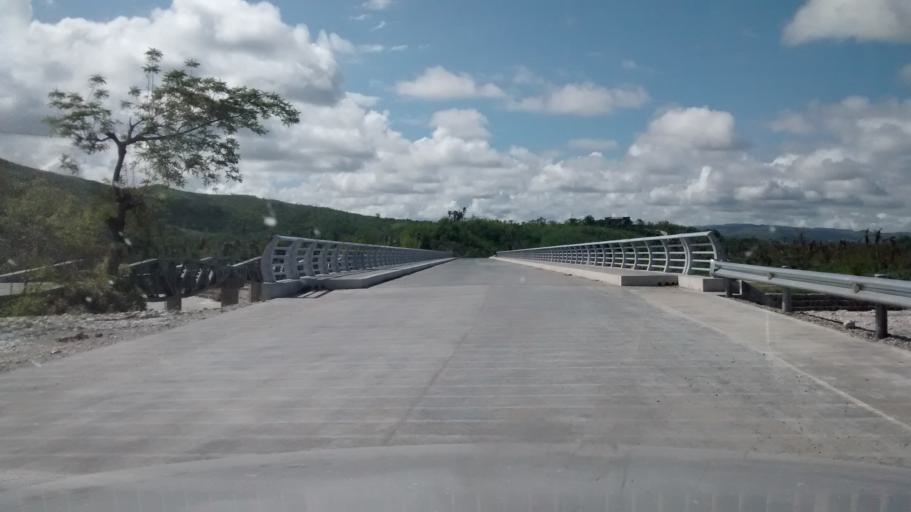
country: HT
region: Grandans
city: Jeremie
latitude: 18.5975
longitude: -74.0301
